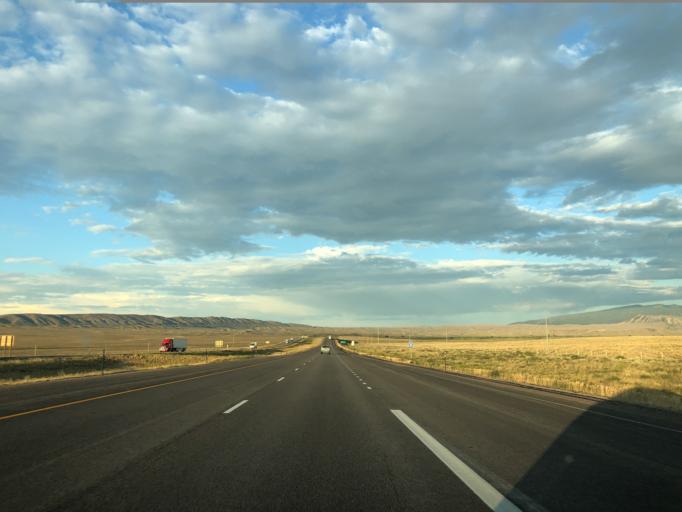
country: US
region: Wyoming
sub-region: Carbon County
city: Saratoga
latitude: 41.7411
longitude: -106.8200
